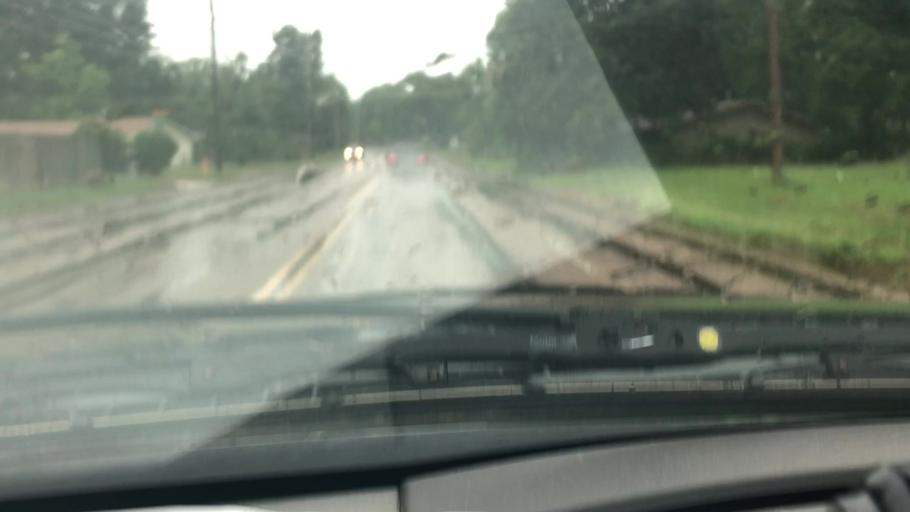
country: US
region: Texas
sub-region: Bowie County
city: Wake Village
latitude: 33.4357
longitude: -94.0878
